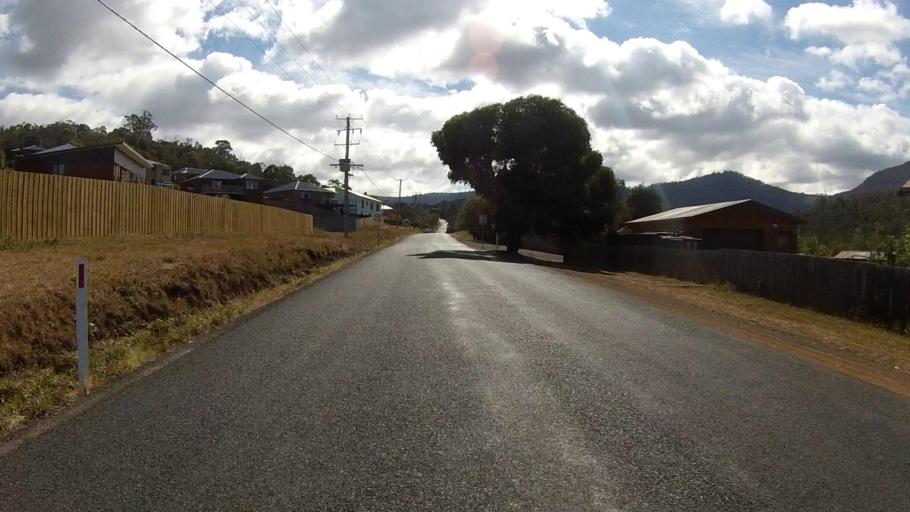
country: AU
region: Tasmania
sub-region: Brighton
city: Old Beach
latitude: -42.7768
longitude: 147.2819
